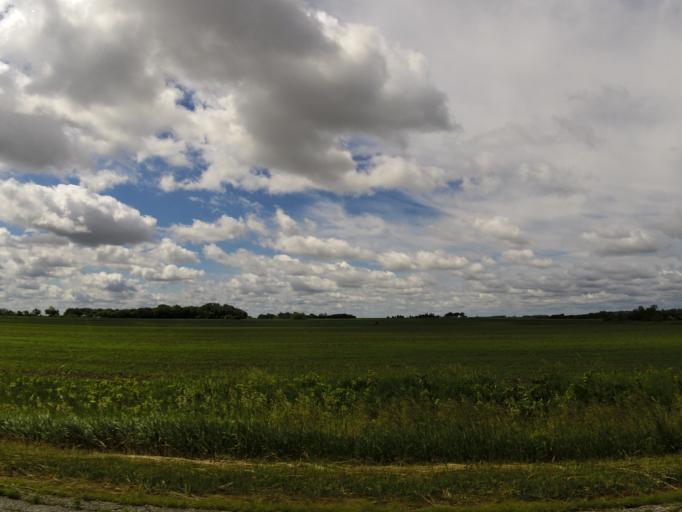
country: US
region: Minnesota
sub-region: Fillmore County
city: Spring Valley
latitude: 43.7109
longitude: -92.4225
